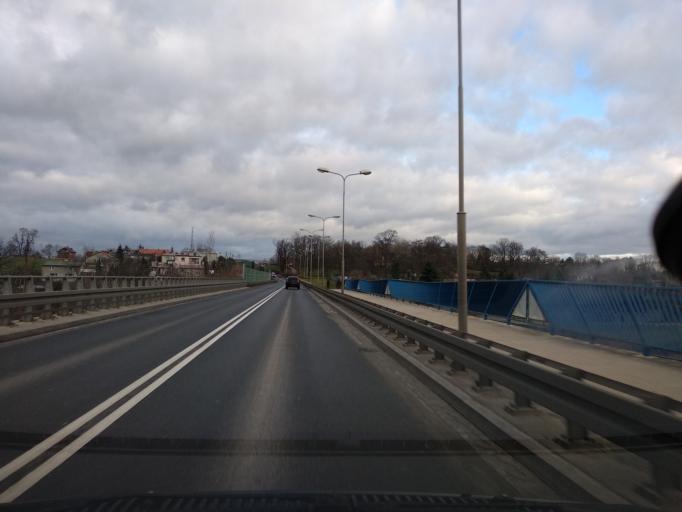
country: PL
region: Greater Poland Voivodeship
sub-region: Kalisz
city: Kalisz
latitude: 51.7729
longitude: 18.0742
